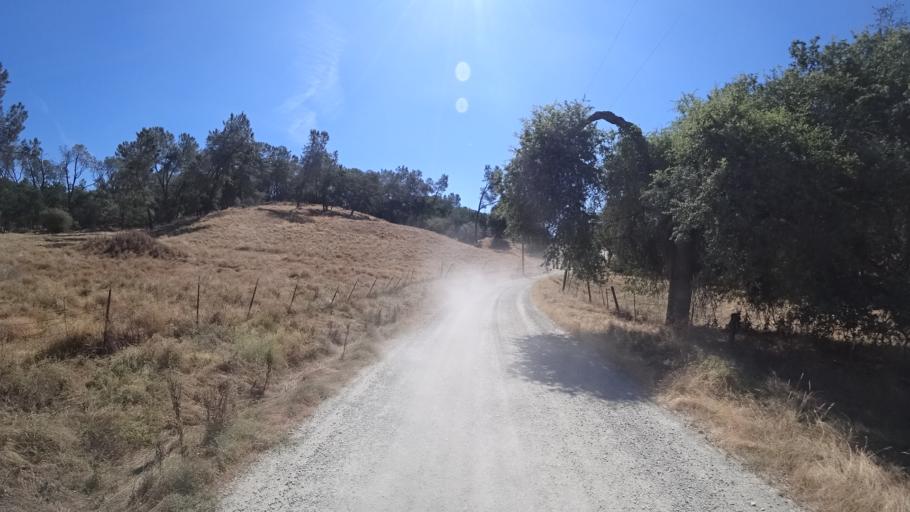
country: US
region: California
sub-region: Calaveras County
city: Valley Springs
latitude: 38.2186
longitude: -120.8763
